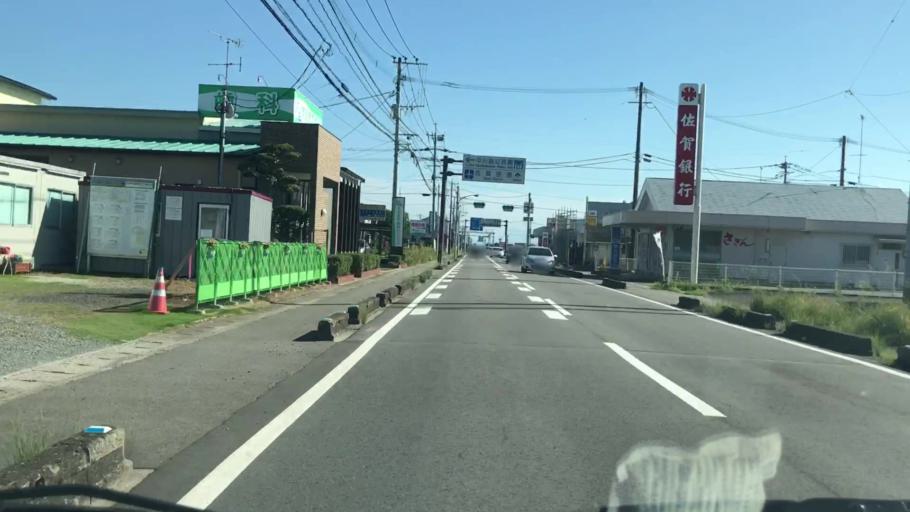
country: JP
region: Saga Prefecture
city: Okawa
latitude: 33.2072
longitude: 130.3353
